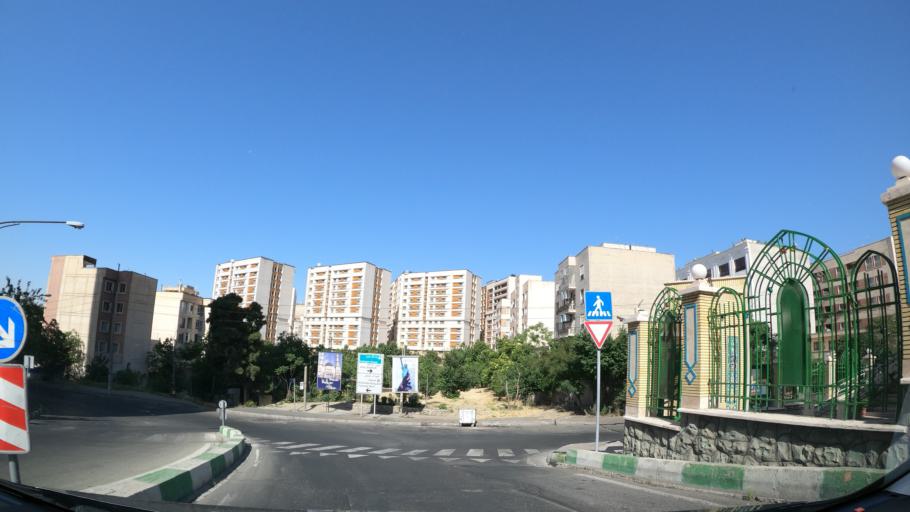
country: IR
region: Tehran
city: Tajrish
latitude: 35.7874
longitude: 51.3886
